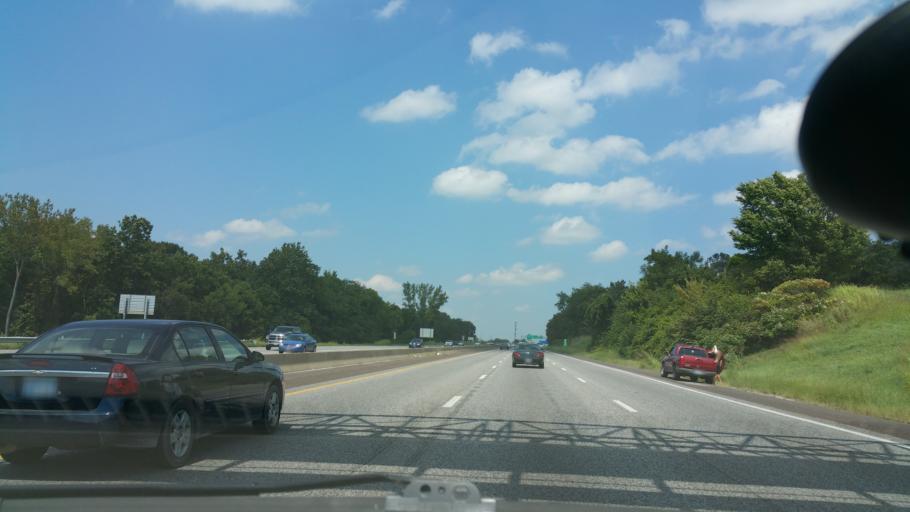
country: US
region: Missouri
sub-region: Clay County
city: North Kansas City
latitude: 39.1569
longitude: -94.5596
